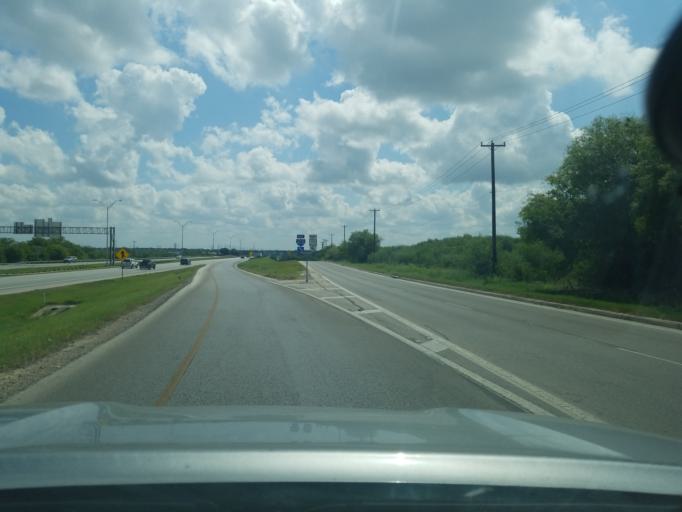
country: US
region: Texas
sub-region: Bexar County
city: San Antonio
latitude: 29.3198
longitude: -98.5220
